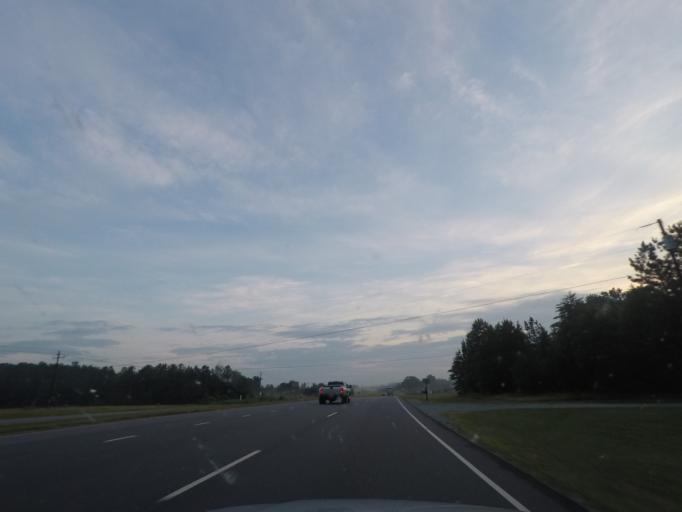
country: US
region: North Carolina
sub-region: Person County
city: Roxboro
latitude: 36.2305
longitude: -78.9315
